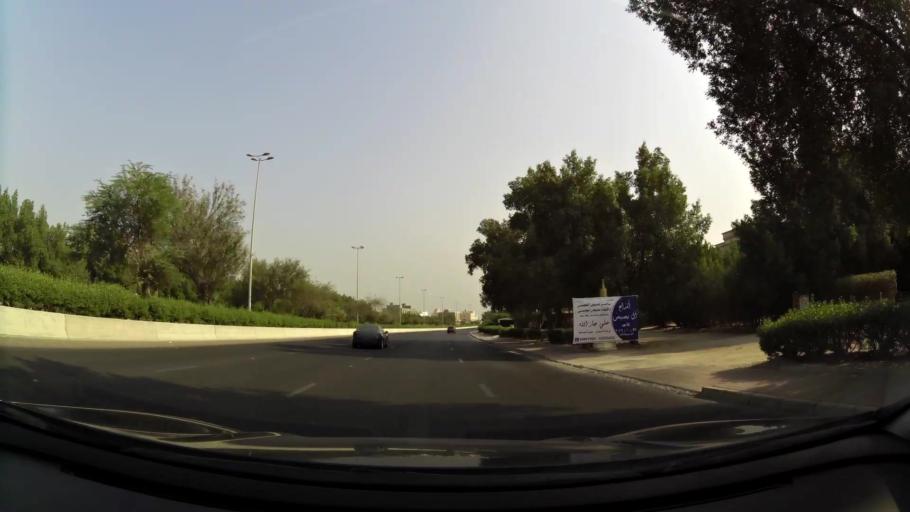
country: KW
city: Al Funaytis
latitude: 29.2236
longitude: 48.0845
